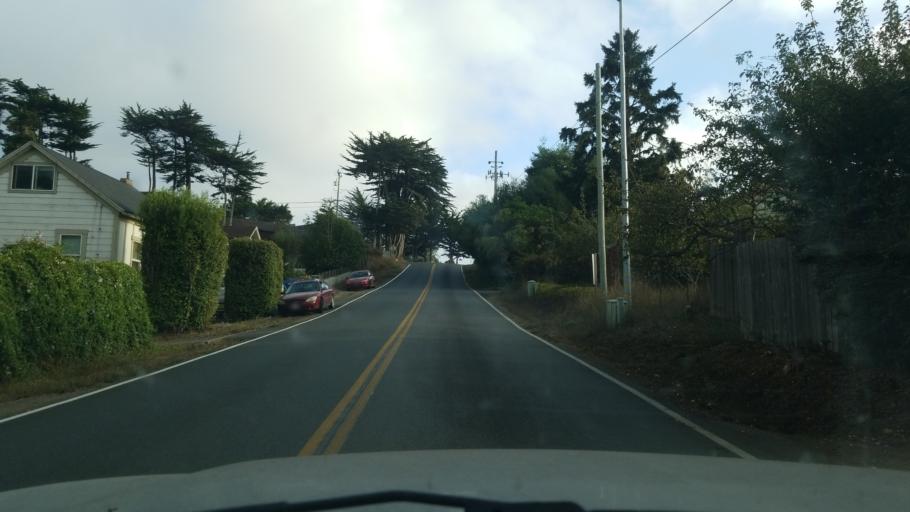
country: US
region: California
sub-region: Mendocino County
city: Fort Bragg
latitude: 39.4207
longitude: -123.8030
